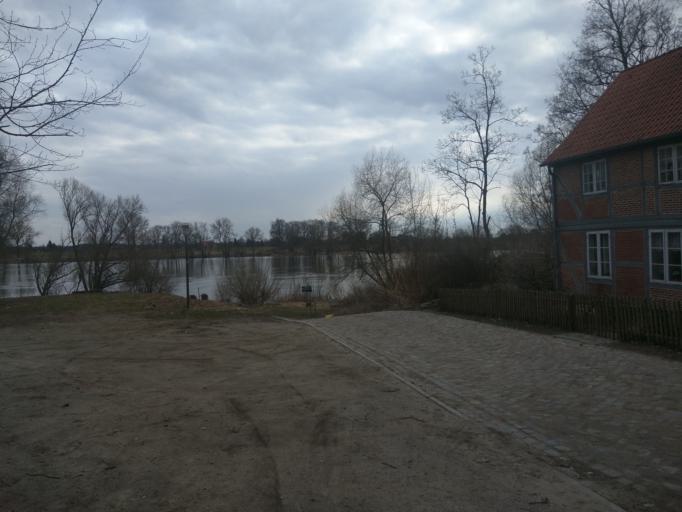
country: DE
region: Schleswig-Holstein
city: Lauenburg
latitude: 53.3718
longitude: 10.5413
